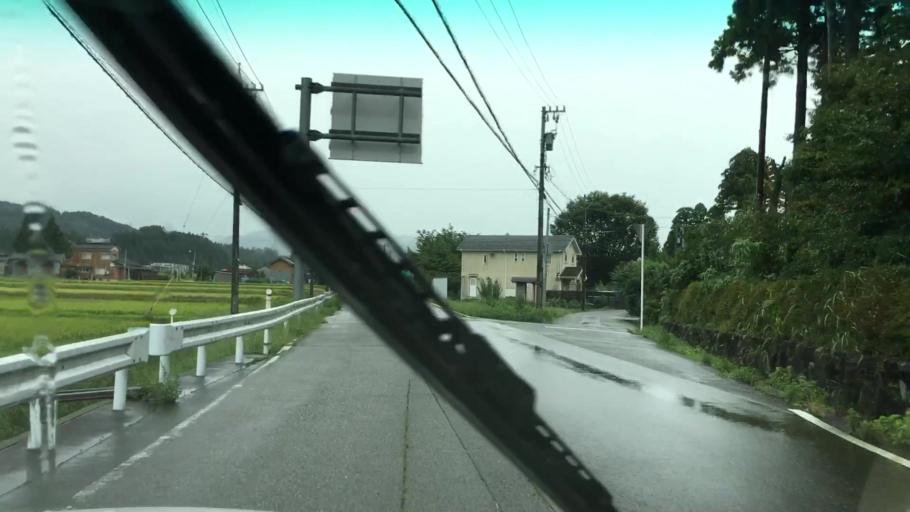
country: JP
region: Toyama
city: Kamiichi
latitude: 36.6248
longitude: 137.3231
